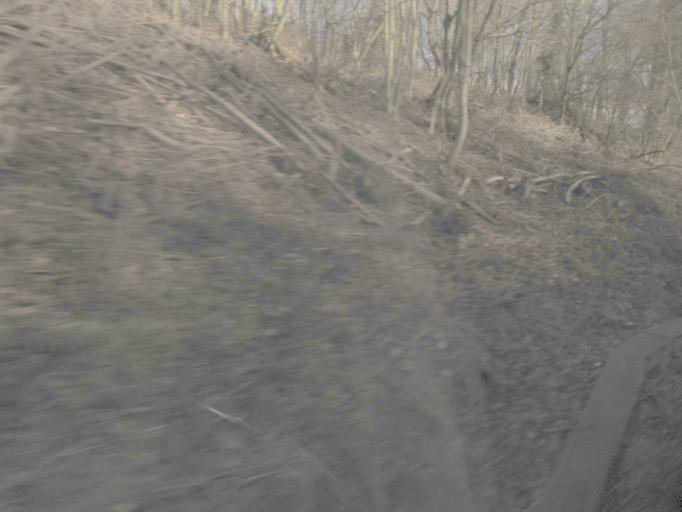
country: GB
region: England
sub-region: Wokingham
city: Sonning
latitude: 51.4601
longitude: -0.9233
